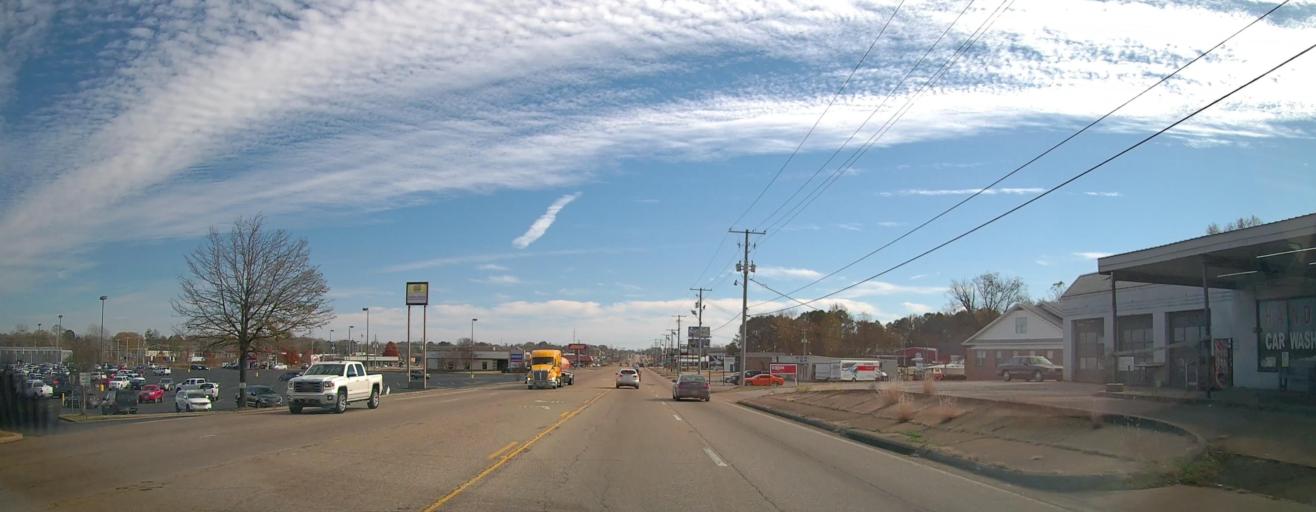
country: US
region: Mississippi
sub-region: Alcorn County
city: Corinth
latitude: 34.9275
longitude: -88.5261
